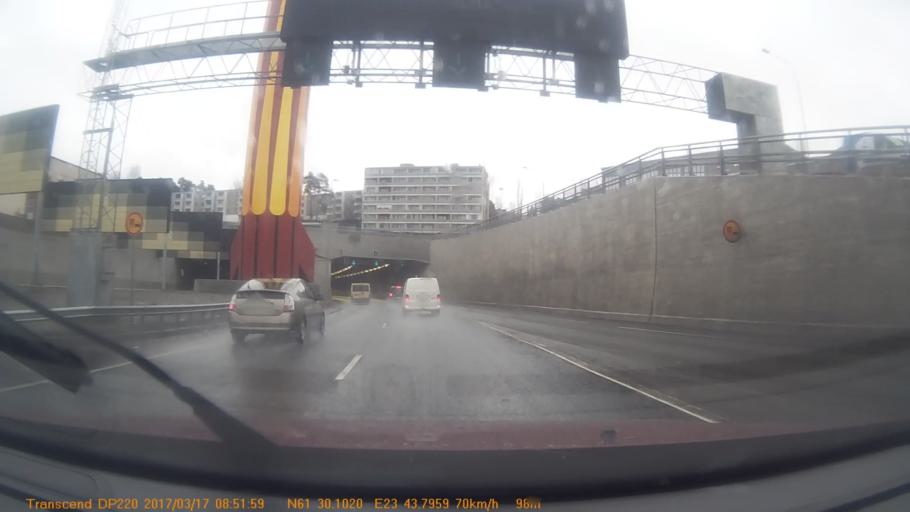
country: FI
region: Pirkanmaa
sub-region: Tampere
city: Tampere
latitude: 61.5018
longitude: 23.7304
